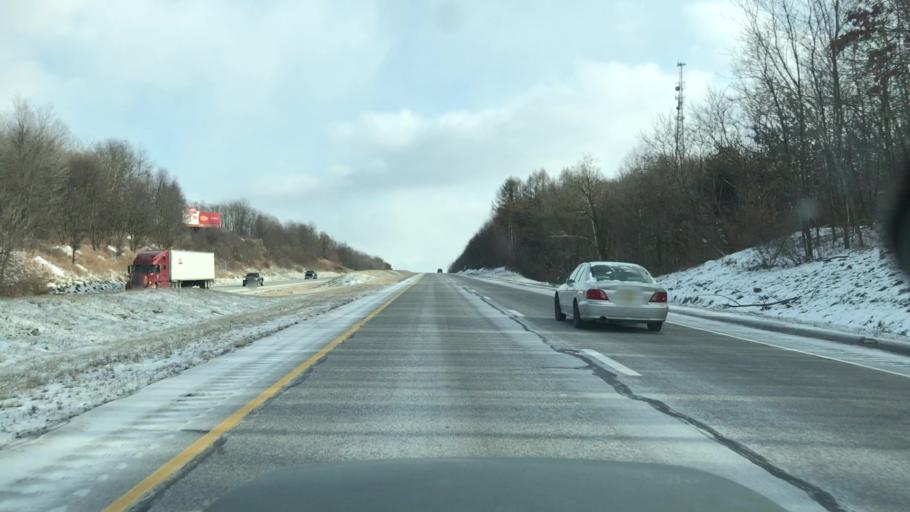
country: US
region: Pennsylvania
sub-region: Jefferson County
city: Brookville
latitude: 41.1865
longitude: -79.1699
